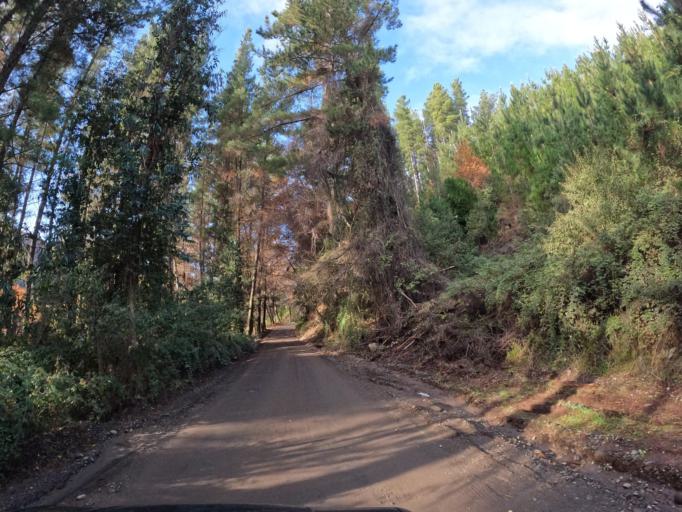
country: CL
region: Biobio
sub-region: Provincia de Nuble
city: Coihueco
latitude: -36.8009
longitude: -71.7121
